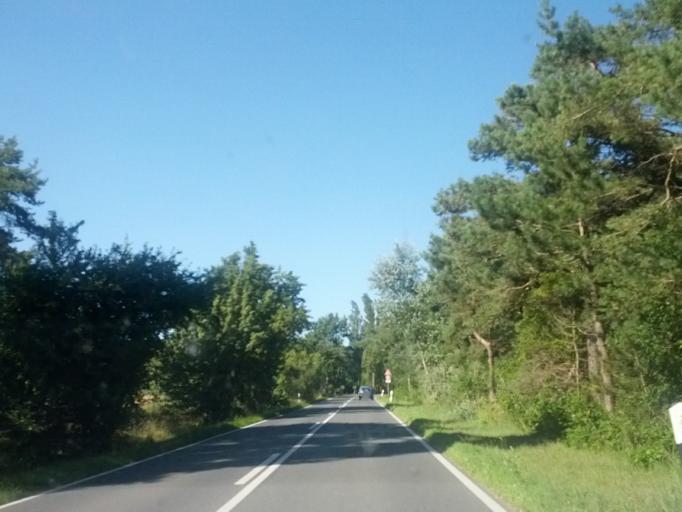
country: DE
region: Mecklenburg-Vorpommern
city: Ostseebad Gohren
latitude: 54.3098
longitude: 13.7158
